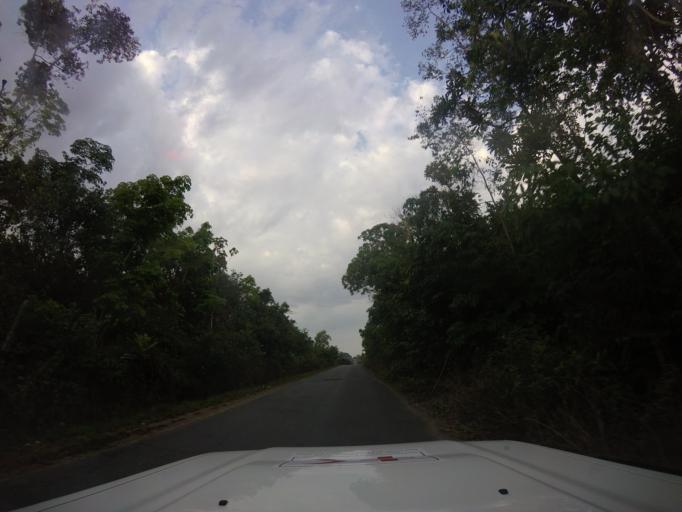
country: LR
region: Bomi
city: Tubmanburg
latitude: 6.7117
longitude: -10.8698
